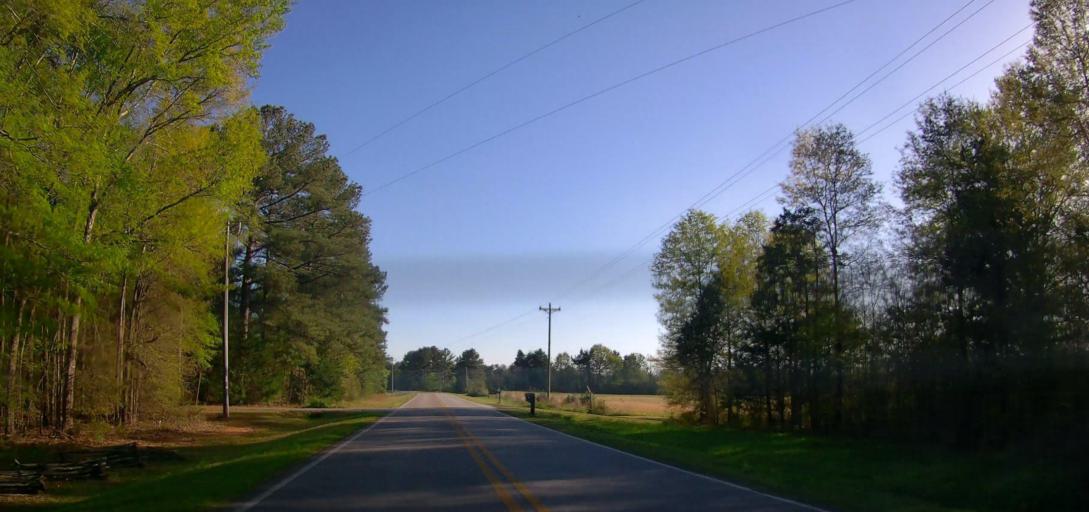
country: US
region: Georgia
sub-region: Butts County
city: Indian Springs
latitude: 33.2838
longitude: -83.8961
